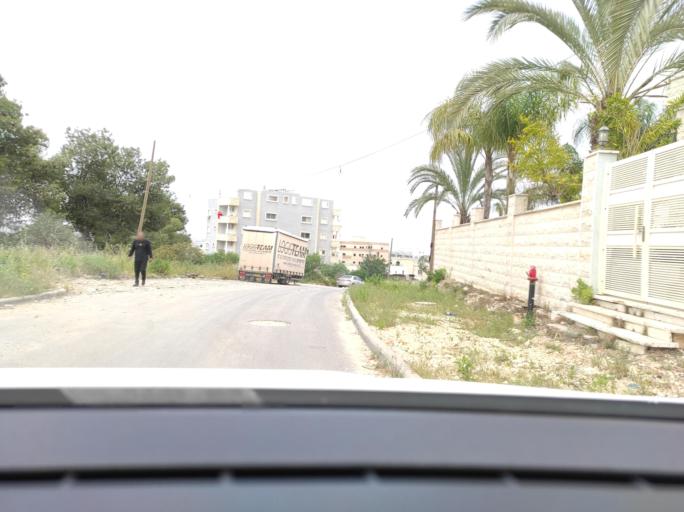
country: IL
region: Central District
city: Kafr Qasim
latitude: 32.1132
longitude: 34.9656
